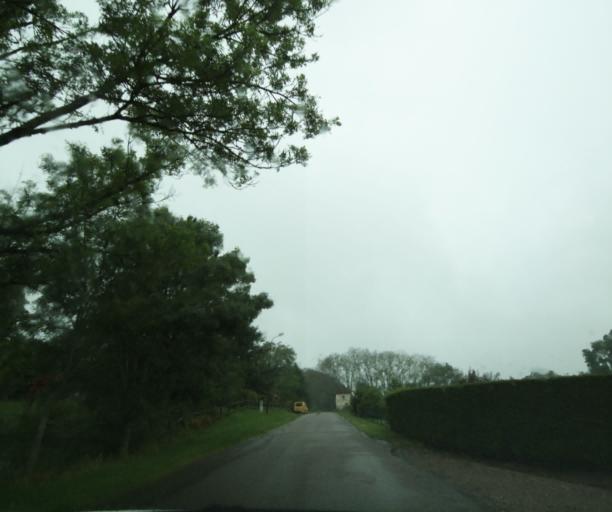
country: FR
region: Bourgogne
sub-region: Departement de Saone-et-Loire
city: Charolles
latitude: 46.3824
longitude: 4.3478
